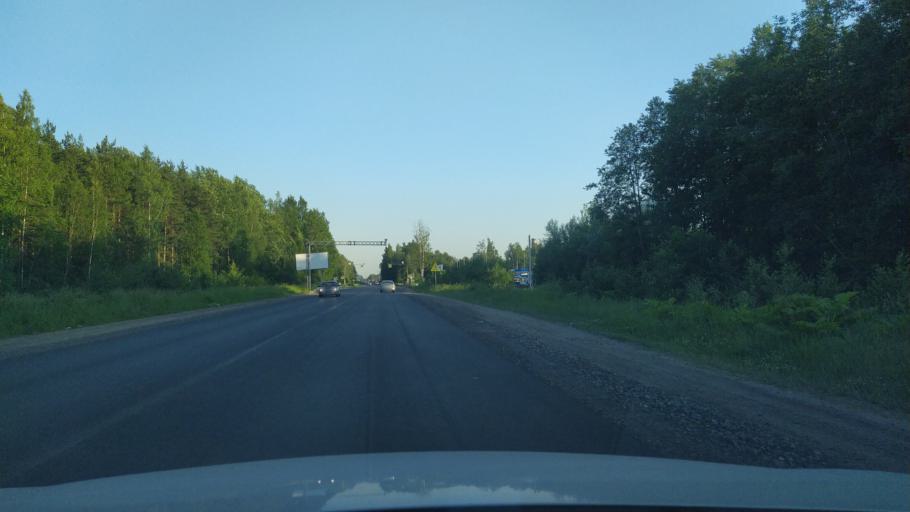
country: RU
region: Leningrad
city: Novoye Devyatkino
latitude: 60.0939
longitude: 30.4981
